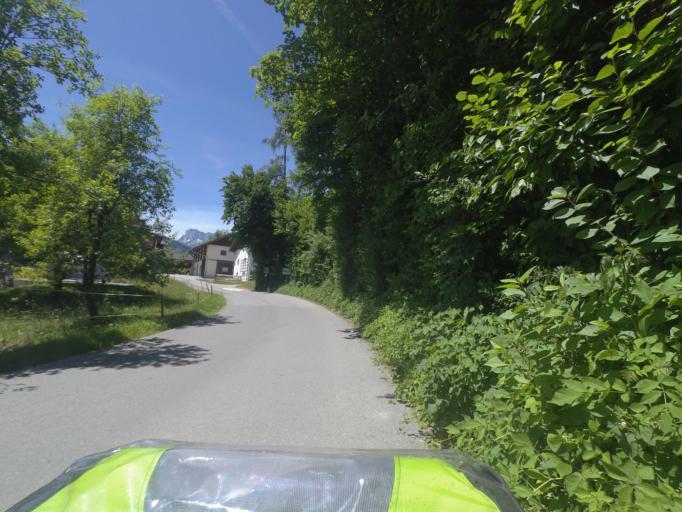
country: AT
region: Salzburg
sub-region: Politischer Bezirk Hallein
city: Oberalm
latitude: 47.7022
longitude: 13.1113
